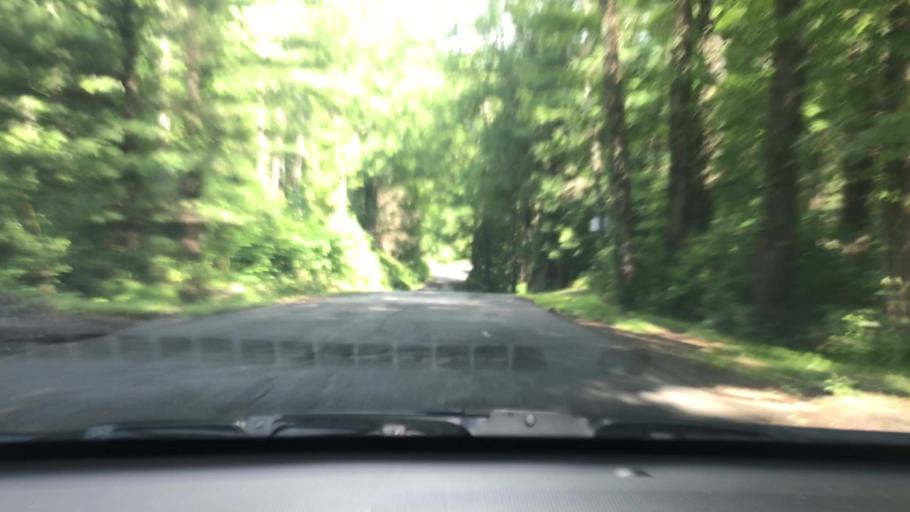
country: US
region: New York
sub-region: Ulster County
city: Shokan
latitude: 41.9651
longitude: -74.2851
